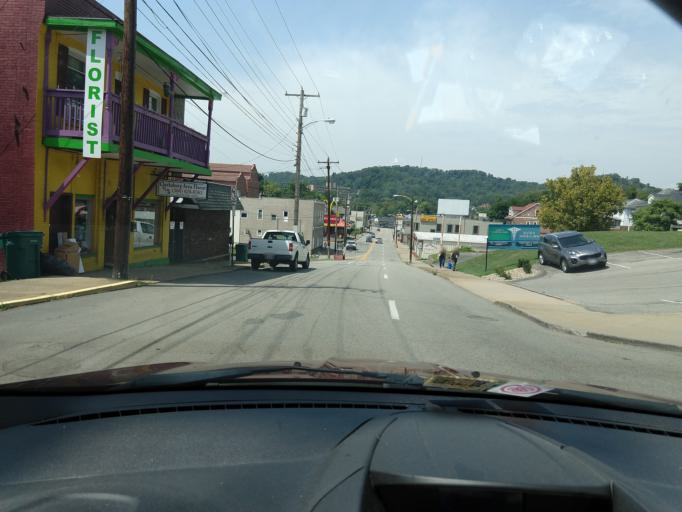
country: US
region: West Virginia
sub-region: Harrison County
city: Clarksburg
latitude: 39.2818
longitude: -80.3465
